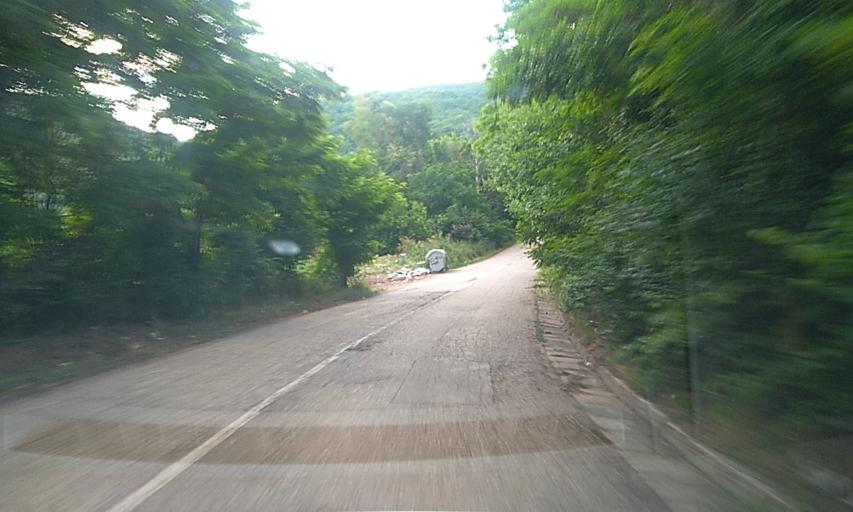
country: RS
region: Central Serbia
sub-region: Nisavski Okrug
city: Niska Banja
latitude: 43.3676
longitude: 21.9883
